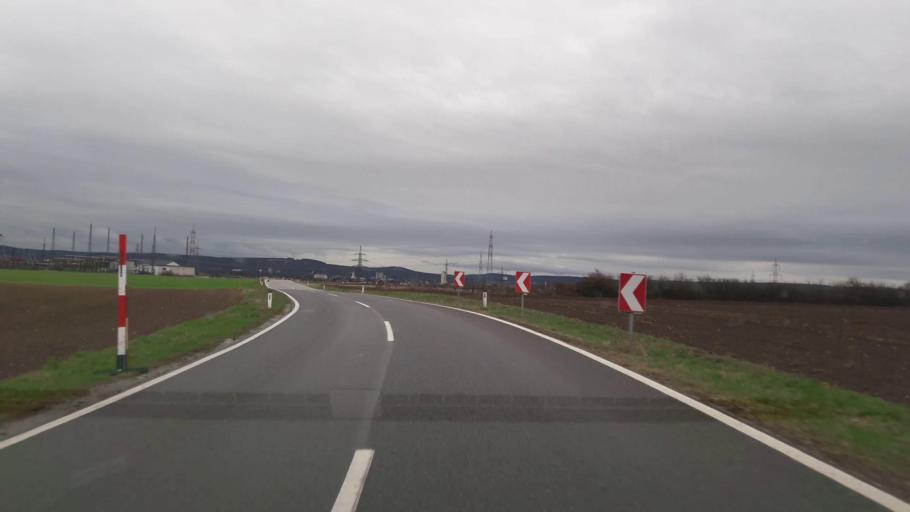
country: AT
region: Lower Austria
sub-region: Politischer Bezirk Bruck an der Leitha
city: Scharndorf
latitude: 48.0511
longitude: 16.7849
